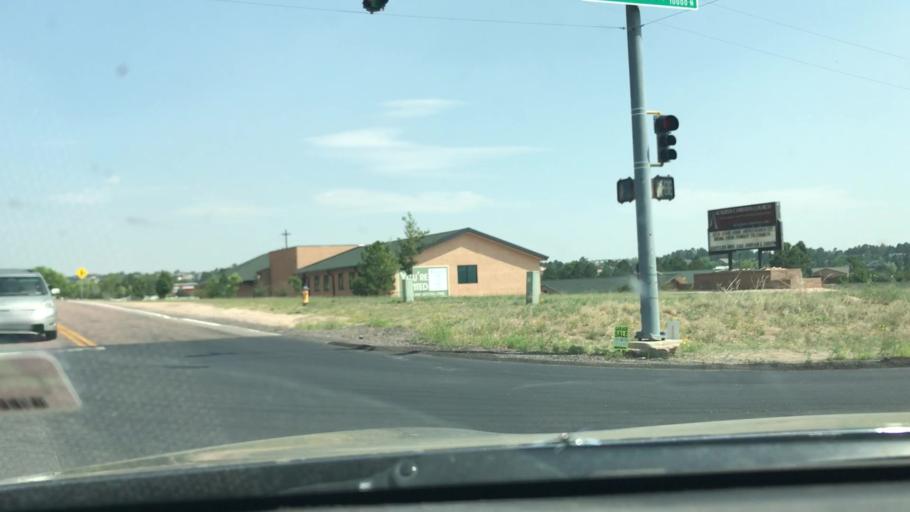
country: US
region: Colorado
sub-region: El Paso County
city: Air Force Academy
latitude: 38.9804
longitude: -104.7977
